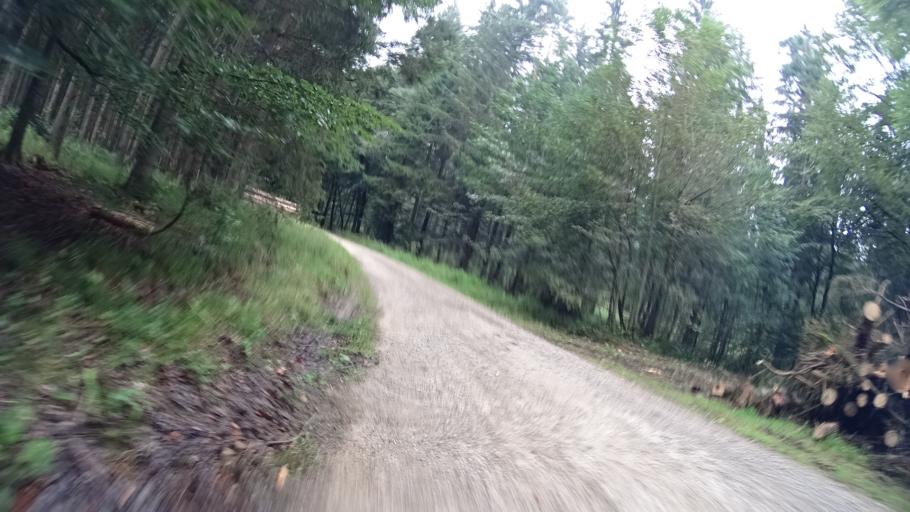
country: DE
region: Bavaria
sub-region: Upper Bavaria
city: Stammham
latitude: 48.8877
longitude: 11.5105
